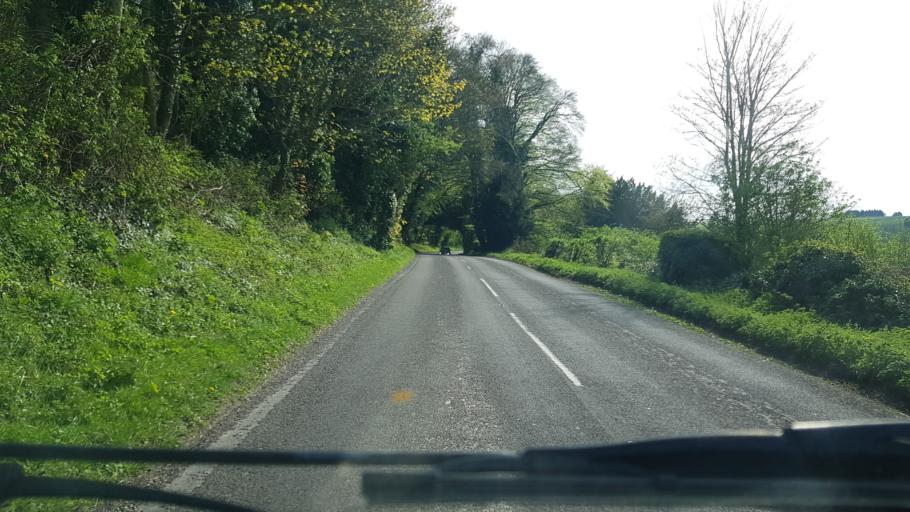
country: GB
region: England
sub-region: Hampshire
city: Kingsclere
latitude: 51.3091
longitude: -1.2558
